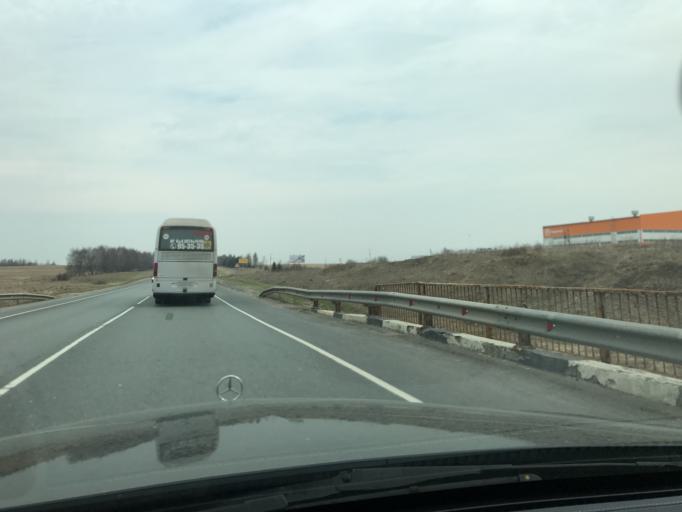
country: RU
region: Vladimir
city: Suzdal'
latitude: 56.3319
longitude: 40.4728
